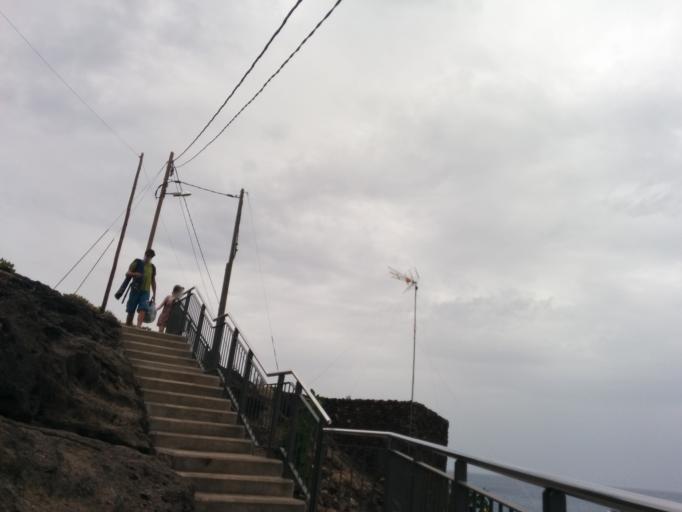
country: ES
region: Canary Islands
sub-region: Provincia de Santa Cruz de Tenerife
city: Adeje
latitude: 28.1126
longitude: -16.7677
